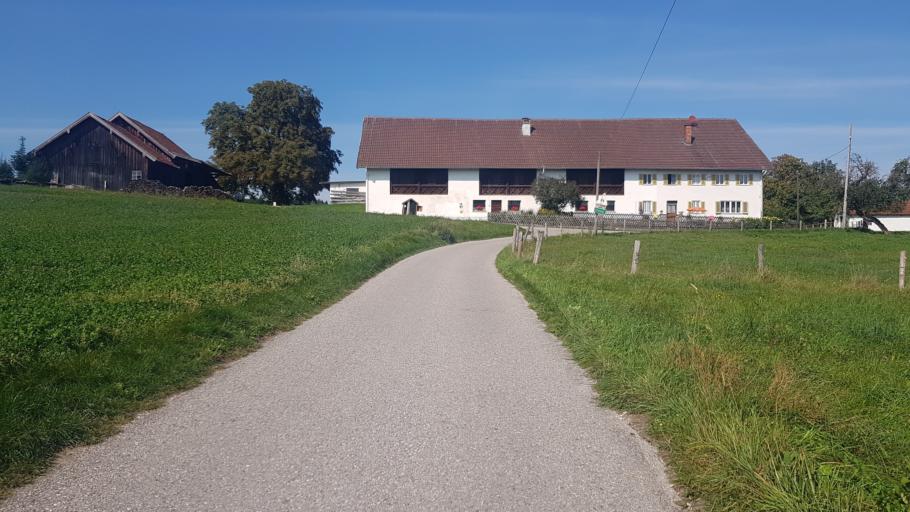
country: DE
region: Bavaria
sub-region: Upper Bavaria
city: Herrsching am Ammersee
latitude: 48.0233
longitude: 11.1595
